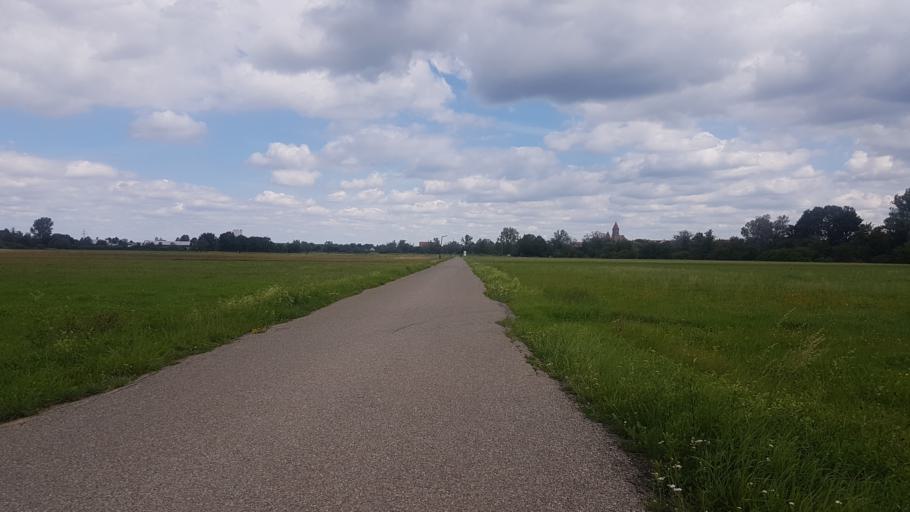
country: DE
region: Bavaria
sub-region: Regierungsbezirk Mittelfranken
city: Gunzenhausen
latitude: 49.1051
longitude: 10.7516
